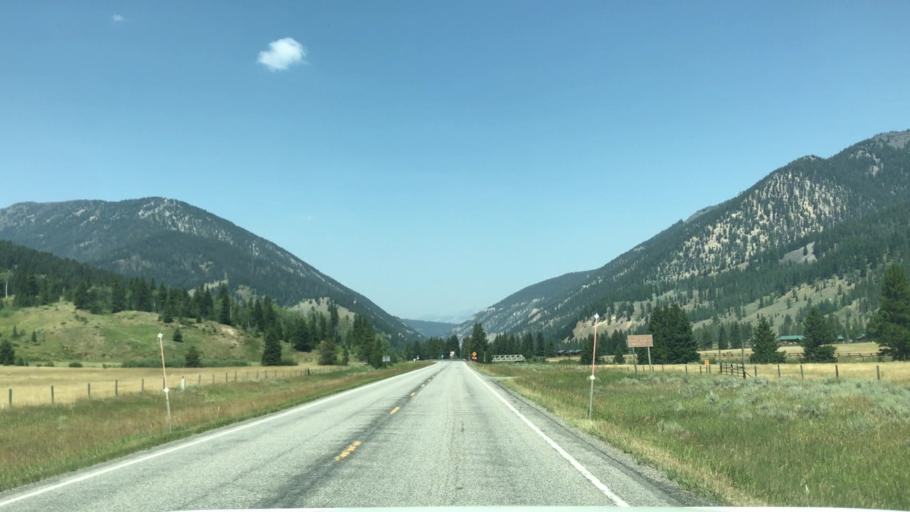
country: US
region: Montana
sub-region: Gallatin County
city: Big Sky
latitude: 45.0973
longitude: -111.2165
